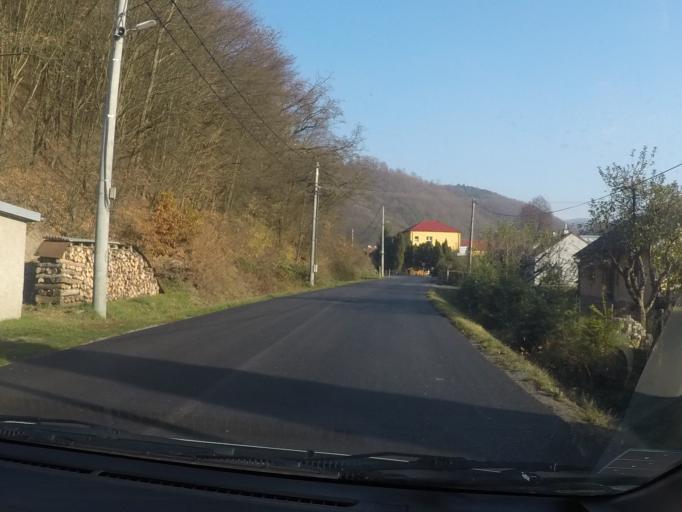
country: SK
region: Banskobystricky
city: Zarnovica
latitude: 48.4610
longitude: 18.7570
